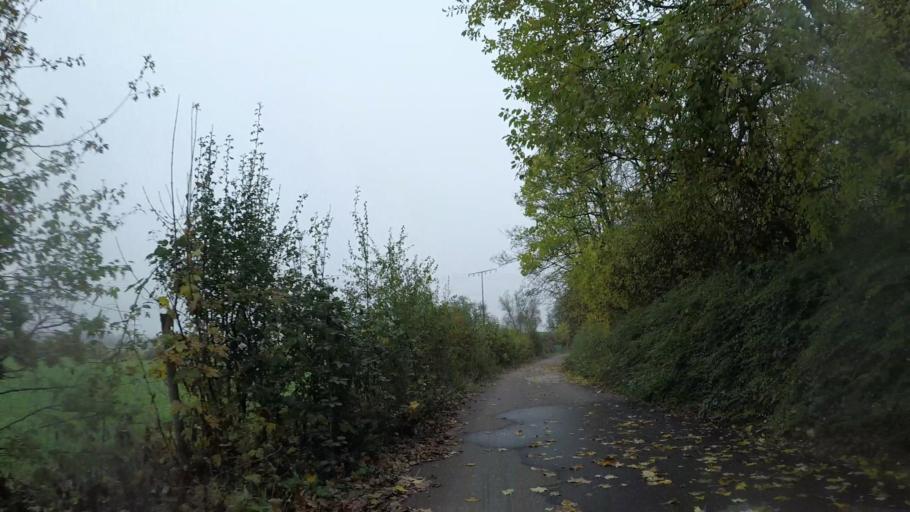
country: DE
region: Baden-Wuerttemberg
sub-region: Tuebingen Region
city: Sickenhausen
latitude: 48.5209
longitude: 9.1954
